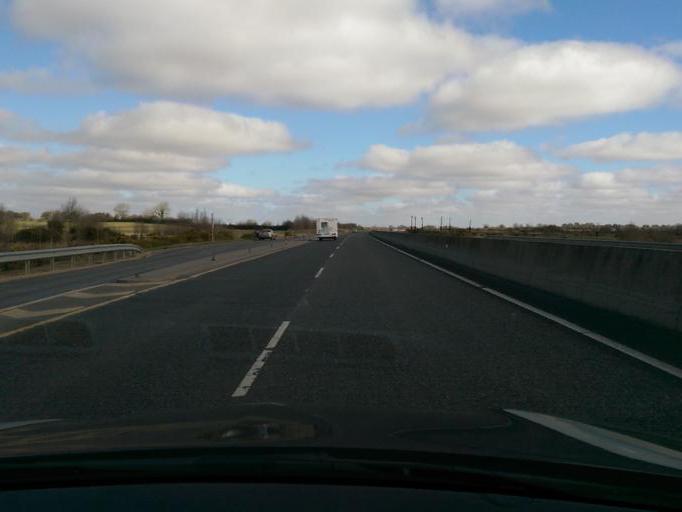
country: IE
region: Leinster
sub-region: An Iarmhi
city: Rochfortbridge
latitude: 53.4374
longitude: -7.2129
